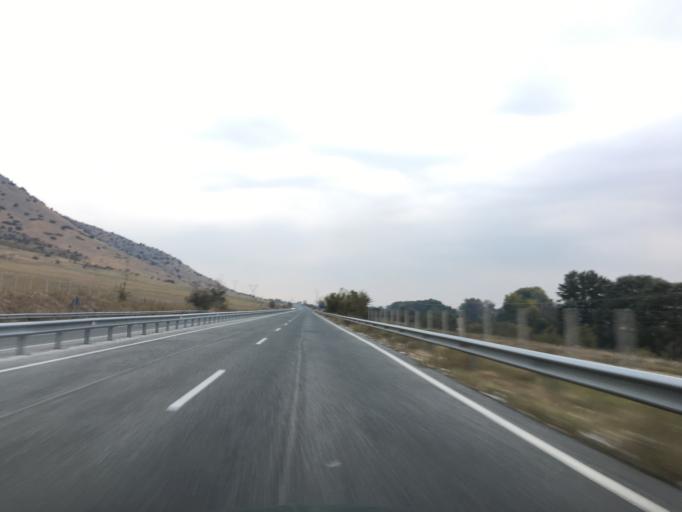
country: GR
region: Thessaly
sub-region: Trikala
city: Zarkos
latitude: 39.5876
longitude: 22.1516
